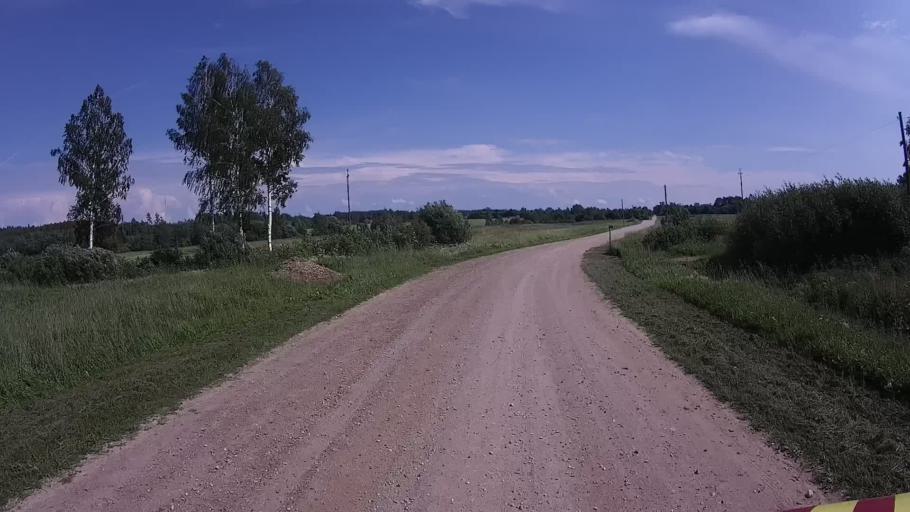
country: EE
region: Viljandimaa
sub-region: Karksi vald
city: Karksi-Nuia
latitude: 58.0012
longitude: 25.5266
